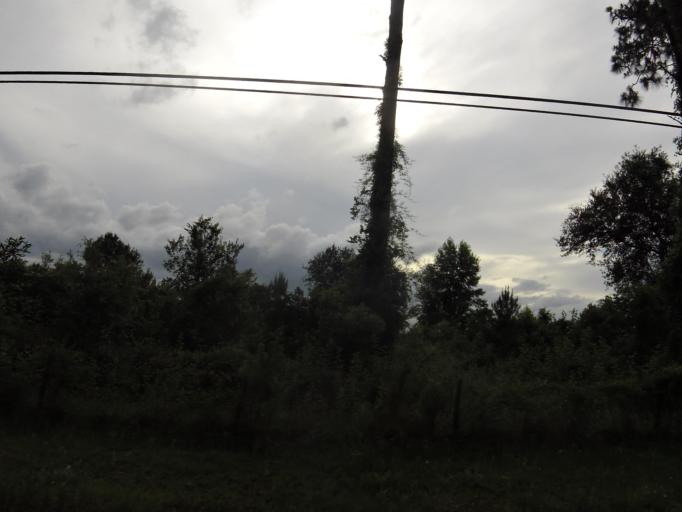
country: US
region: Florida
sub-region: Nassau County
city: Nassau Village-Ratliff
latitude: 30.5170
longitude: -81.7478
